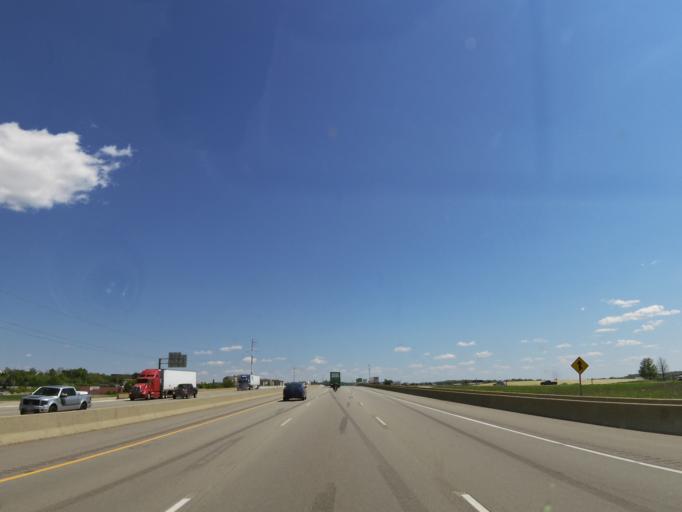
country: US
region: Wisconsin
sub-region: Dane County
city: Maple Bluff
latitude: 43.1396
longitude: -89.2980
